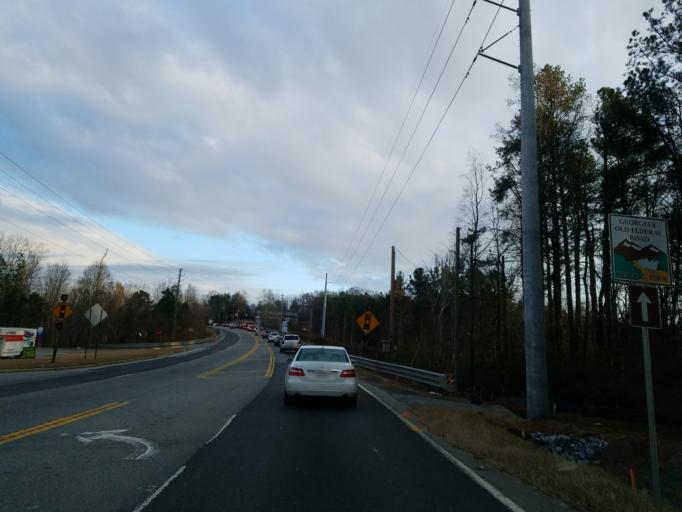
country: US
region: Georgia
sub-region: Forsyth County
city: Cumming
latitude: 34.2648
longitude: -84.0898
